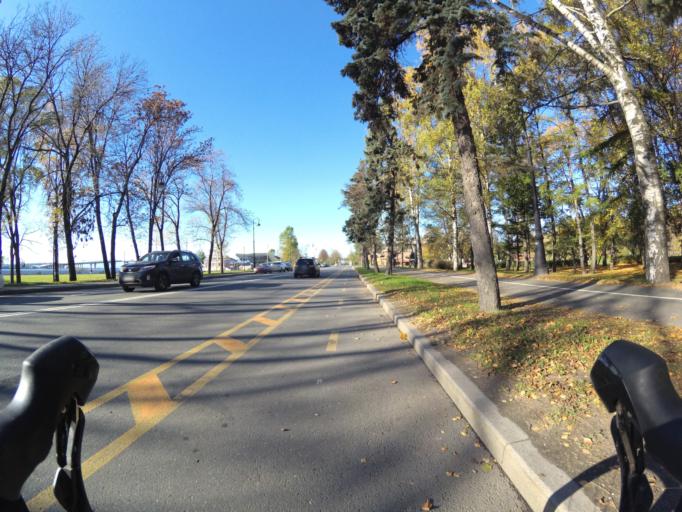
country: RU
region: St.-Petersburg
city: Staraya Derevnya
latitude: 59.9688
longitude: 30.2357
